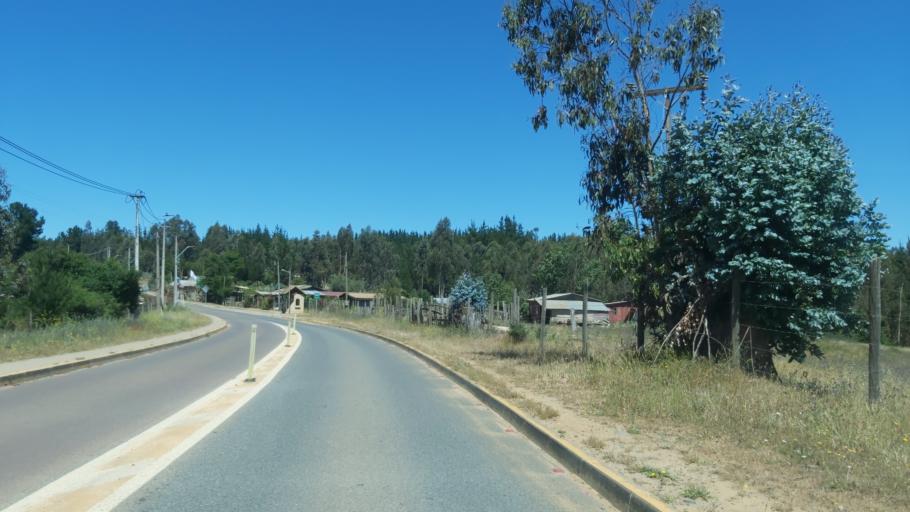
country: CL
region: Maule
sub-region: Provincia de Talca
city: Talca
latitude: -34.9640
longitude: -71.9620
